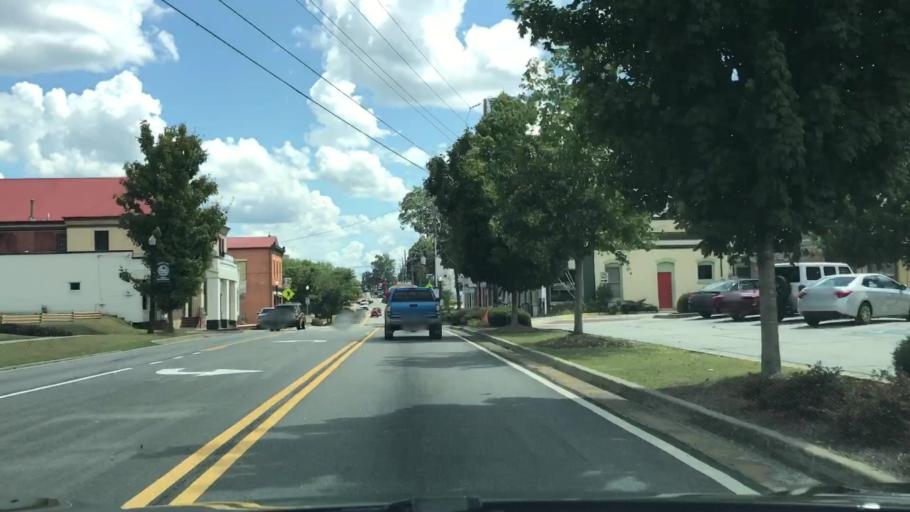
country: US
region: Georgia
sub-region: Oconee County
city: Watkinsville
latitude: 33.8638
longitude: -83.4097
